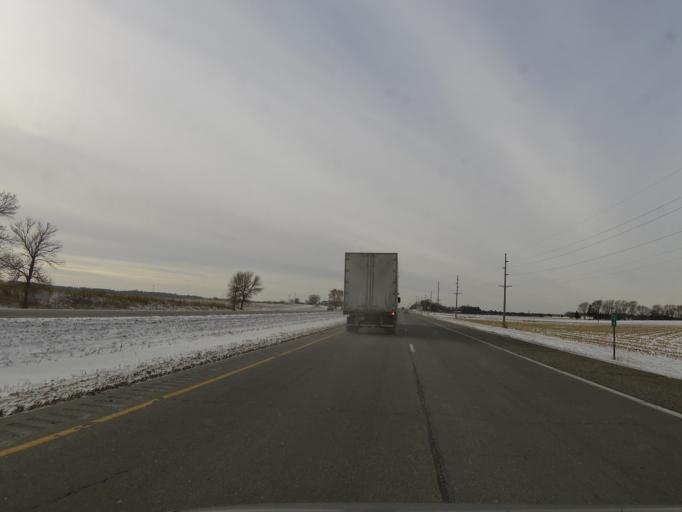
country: US
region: Minnesota
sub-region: Scott County
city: Belle Plaine
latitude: 44.6377
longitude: -93.7218
